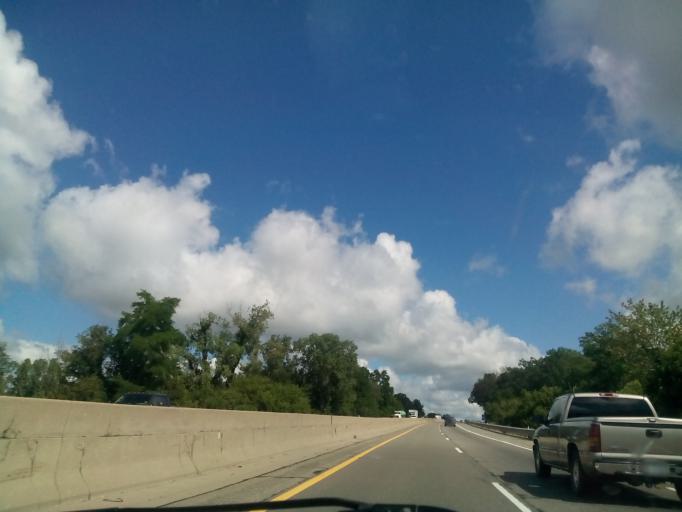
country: US
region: Michigan
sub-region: Livingston County
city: Brighton
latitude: 42.6609
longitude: -83.7591
